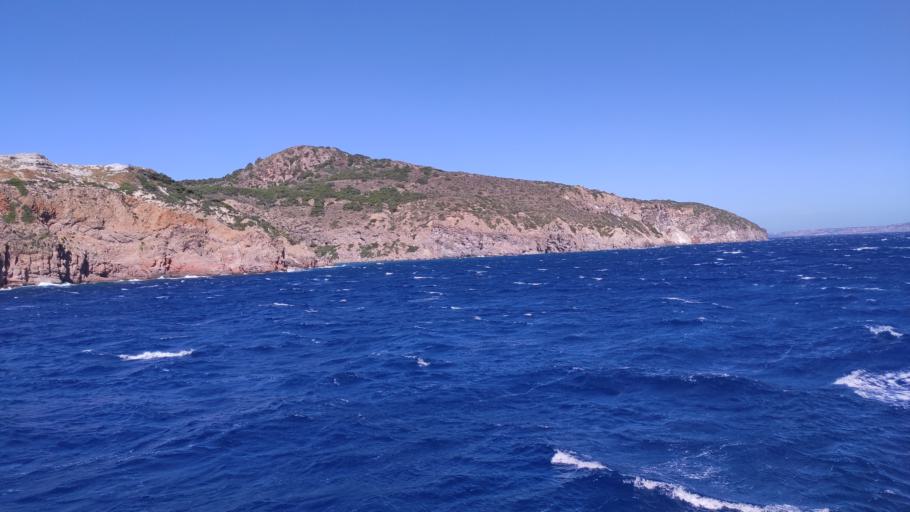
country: GR
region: South Aegean
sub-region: Nomos Dodekanisou
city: Mandraki
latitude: 36.6717
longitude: 27.1475
